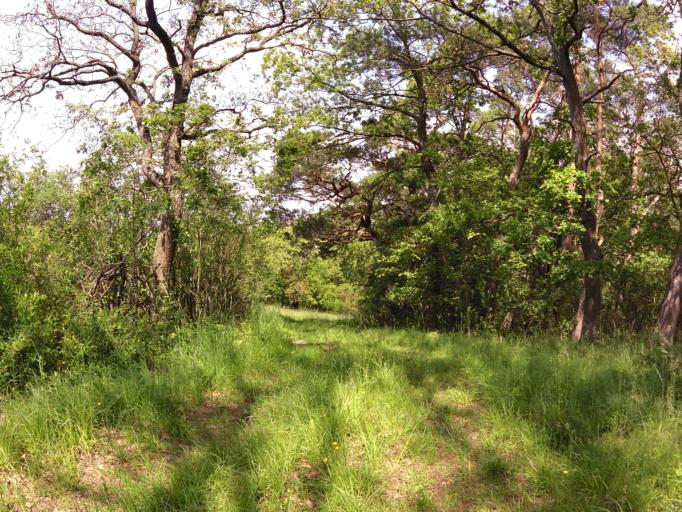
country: DE
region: Bavaria
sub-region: Regierungsbezirk Unterfranken
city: Winterhausen
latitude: 49.7190
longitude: 10.0229
